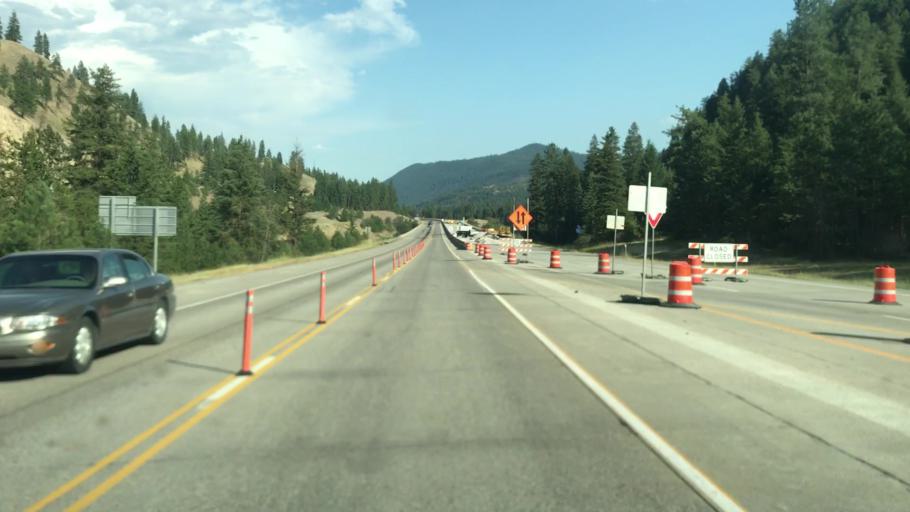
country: US
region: Montana
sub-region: Mineral County
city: Superior
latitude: 47.2233
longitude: -114.9650
